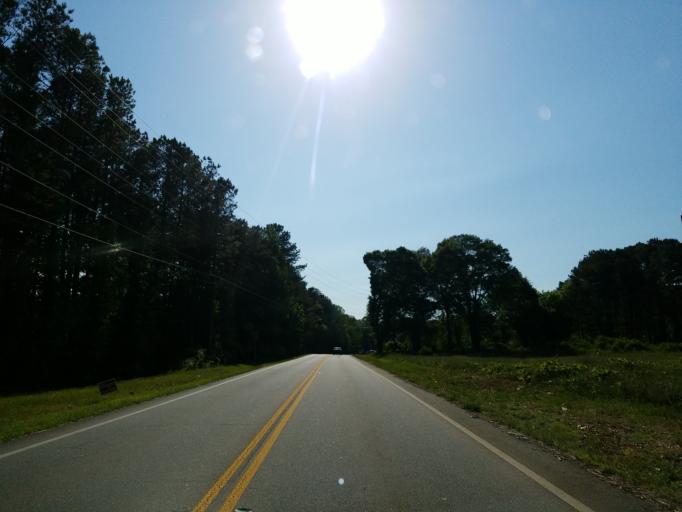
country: US
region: Georgia
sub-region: Paulding County
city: Hiram
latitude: 33.9177
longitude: -84.7754
